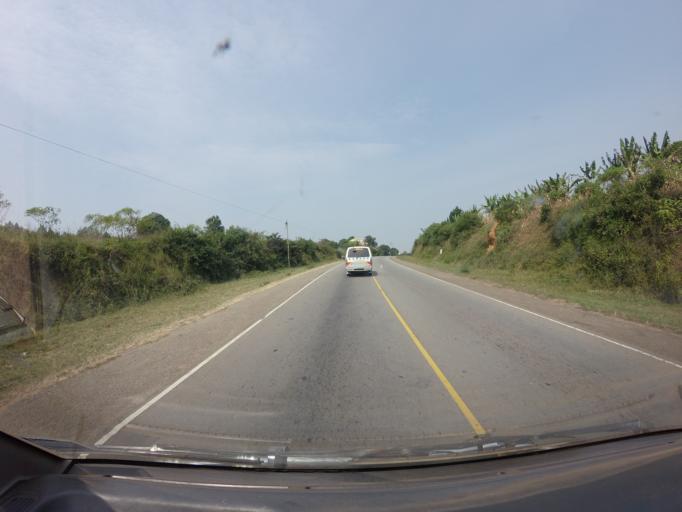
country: UG
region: Central Region
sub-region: Lwengo District
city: Lwengo
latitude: -0.3959
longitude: 31.4195
